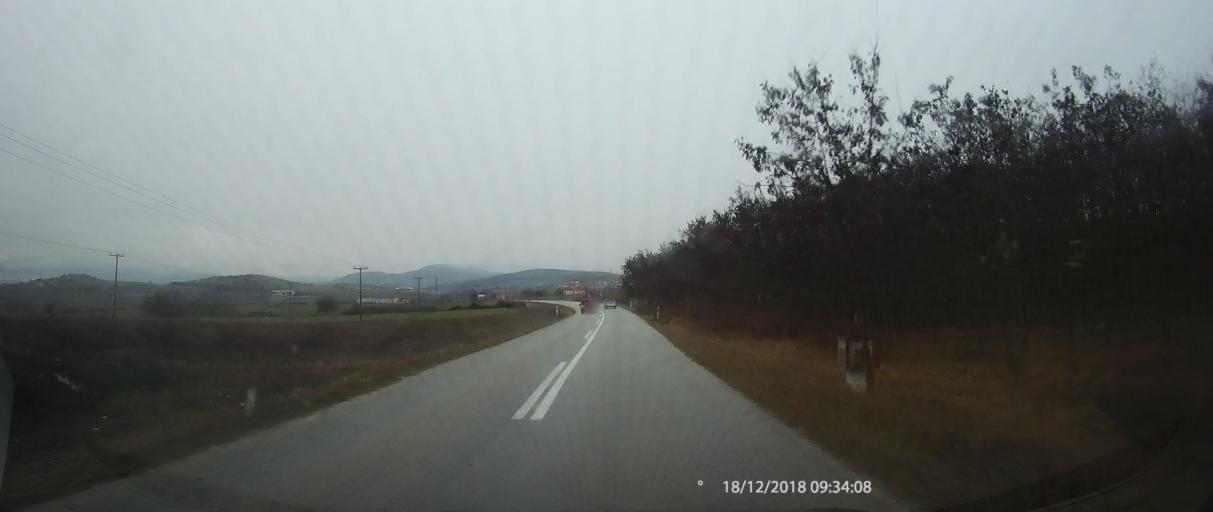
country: GR
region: Thessaly
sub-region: Nomos Larisis
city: Elassona
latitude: 39.9694
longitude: 22.1806
